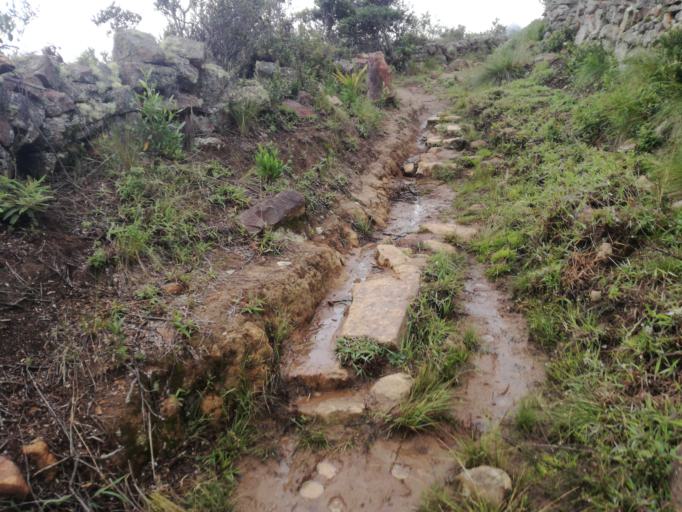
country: CO
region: Boyaca
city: Socha Viejo
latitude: 6.0030
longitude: -72.6847
